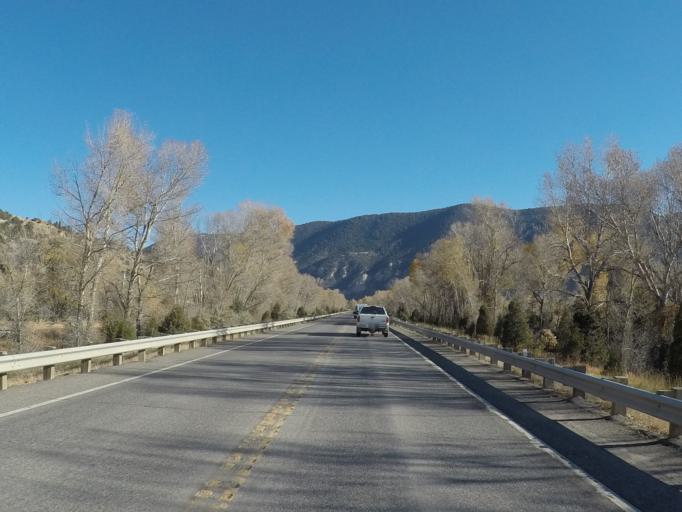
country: US
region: Montana
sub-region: Park County
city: Livingston
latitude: 45.5787
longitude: -110.5822
